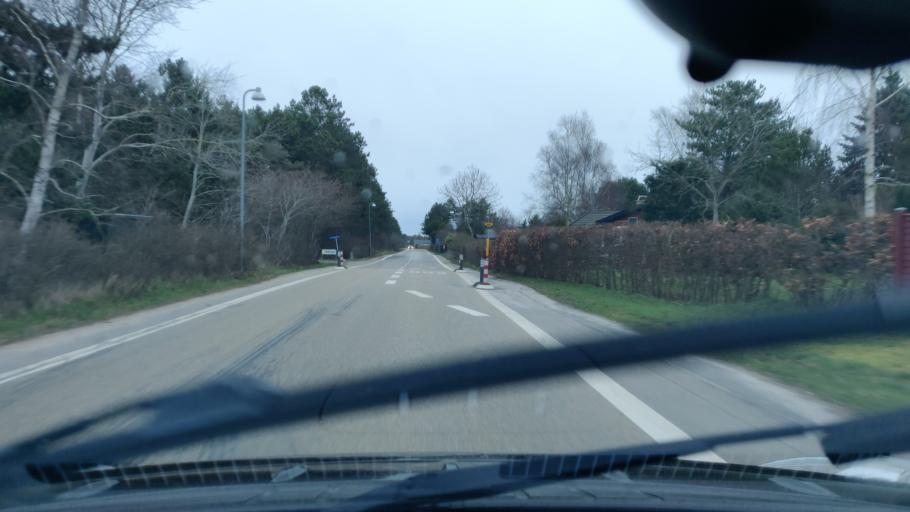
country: DK
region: Zealand
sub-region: Odsherred Kommune
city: Asnaes
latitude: 55.8652
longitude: 11.5341
